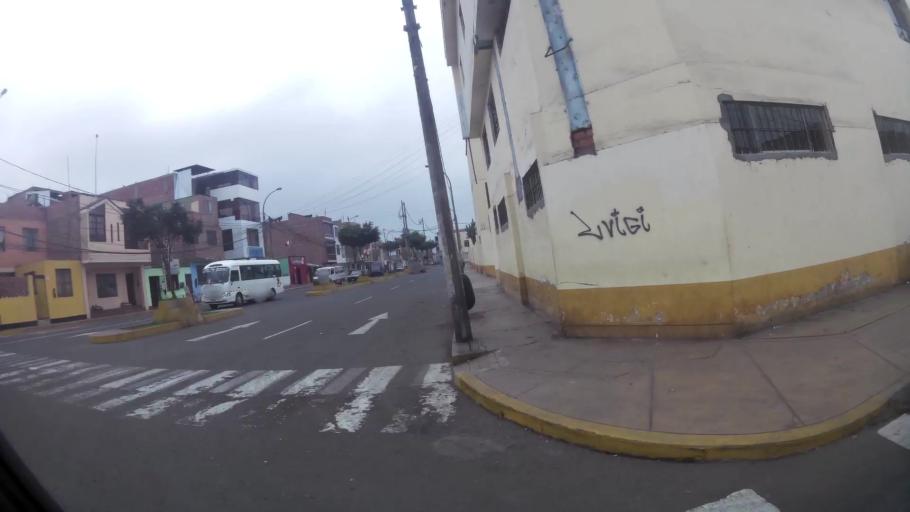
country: PE
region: Lima
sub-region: Provincia de Huaral
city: Chancay
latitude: -11.5601
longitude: -77.2708
